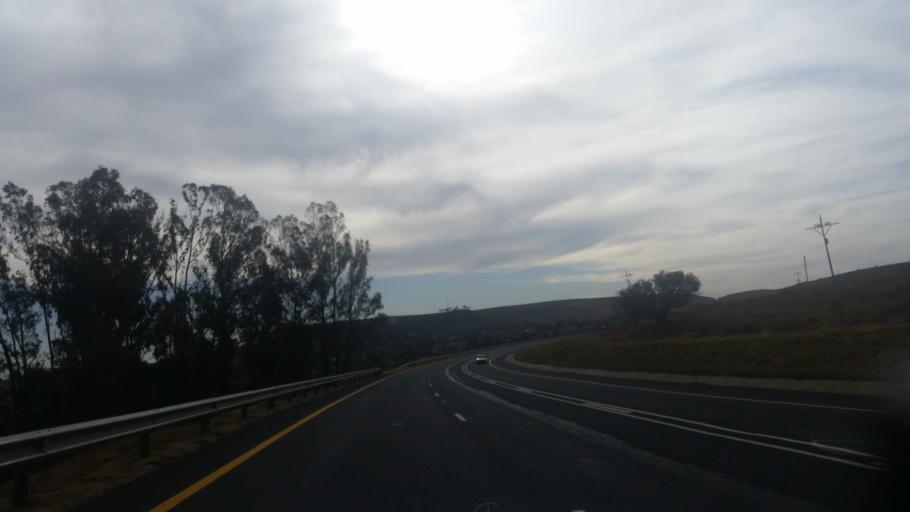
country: ZA
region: Orange Free State
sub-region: Thabo Mofutsanyana District Municipality
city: Phuthaditjhaba
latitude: -28.3134
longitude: 28.7201
